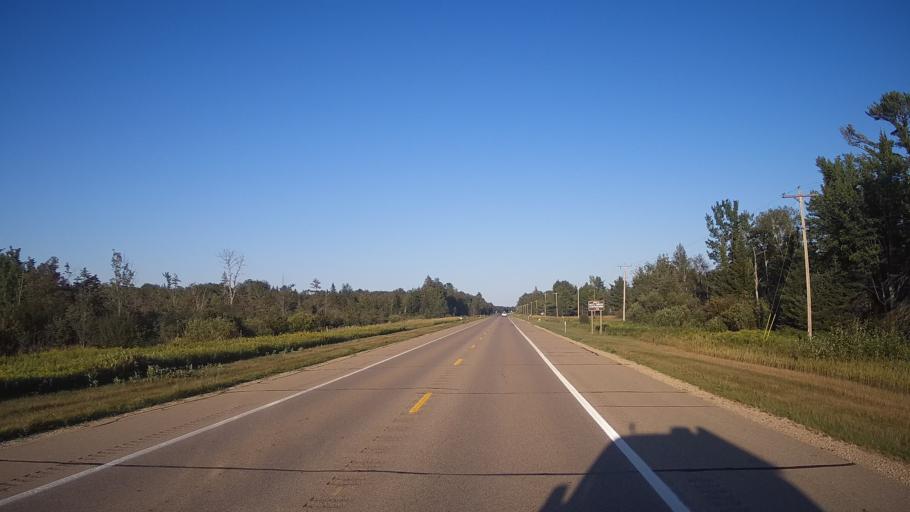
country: US
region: Michigan
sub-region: Delta County
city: Gladstone
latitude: 45.8955
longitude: -86.7283
